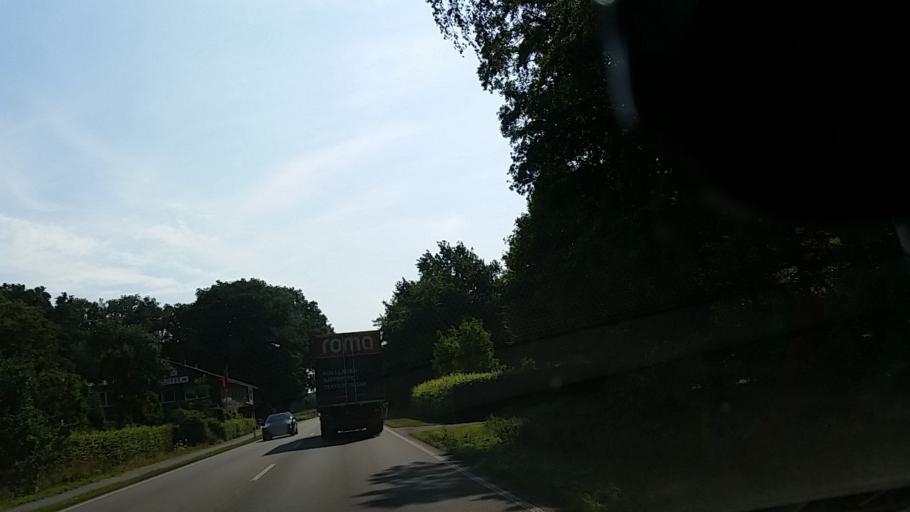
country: DE
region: Lower Saxony
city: Steinfeld
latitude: 52.5944
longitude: 8.2501
